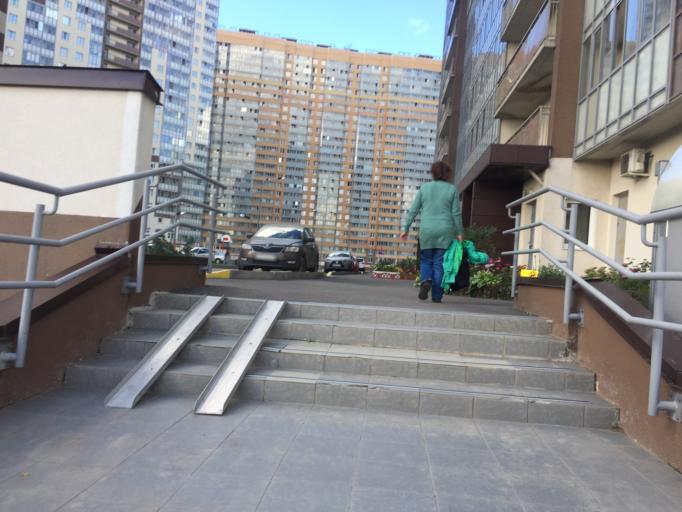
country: RU
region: Leningrad
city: Murino
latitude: 60.0482
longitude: 30.4356
